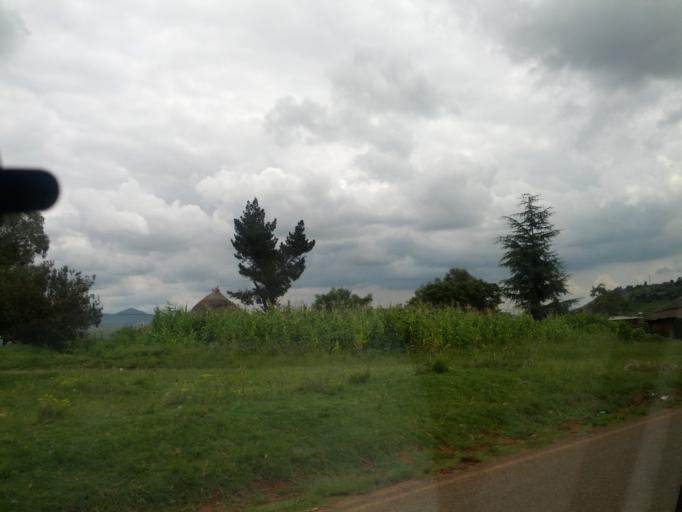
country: LS
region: Leribe
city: Leribe
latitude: -29.0086
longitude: 28.2142
